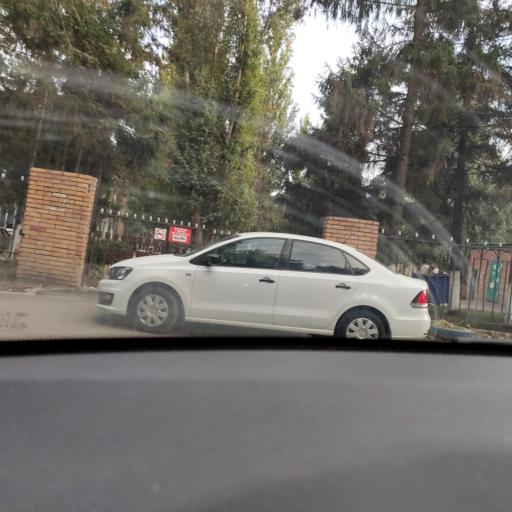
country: RU
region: Samara
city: Samara
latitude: 53.2150
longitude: 50.2405
